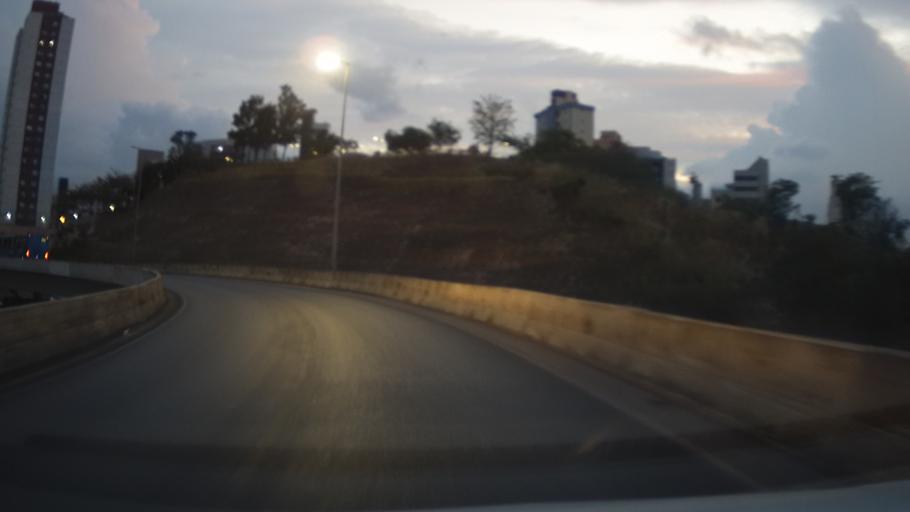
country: BR
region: Minas Gerais
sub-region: Belo Horizonte
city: Belo Horizonte
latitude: -19.8946
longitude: -43.9273
